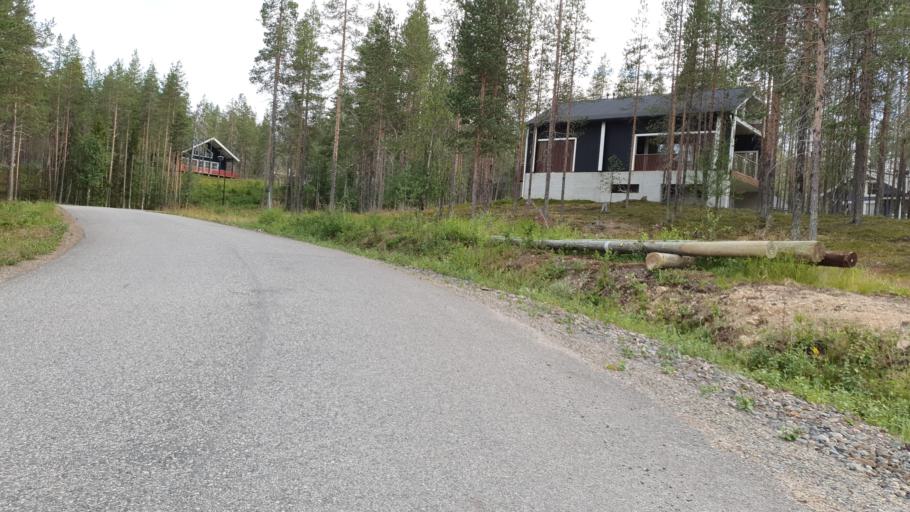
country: FI
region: Lapland
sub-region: Tunturi-Lappi
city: Kolari
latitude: 67.5930
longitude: 24.1294
